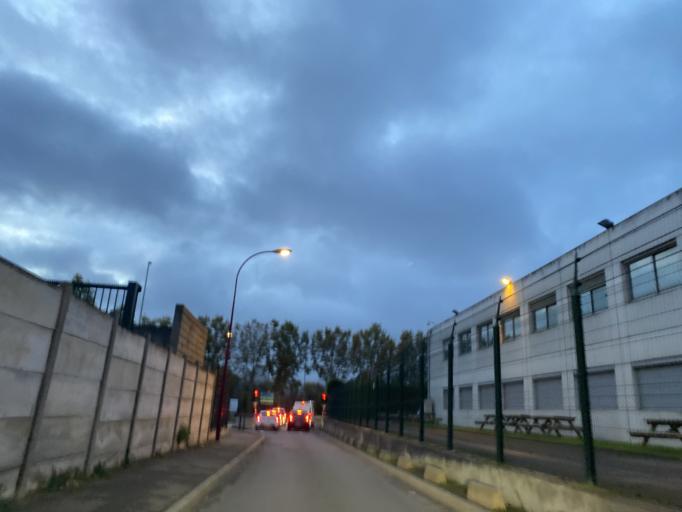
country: FR
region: Ile-de-France
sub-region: Departement du Val-d'Oise
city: Bezons
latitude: 48.9256
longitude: 2.2242
